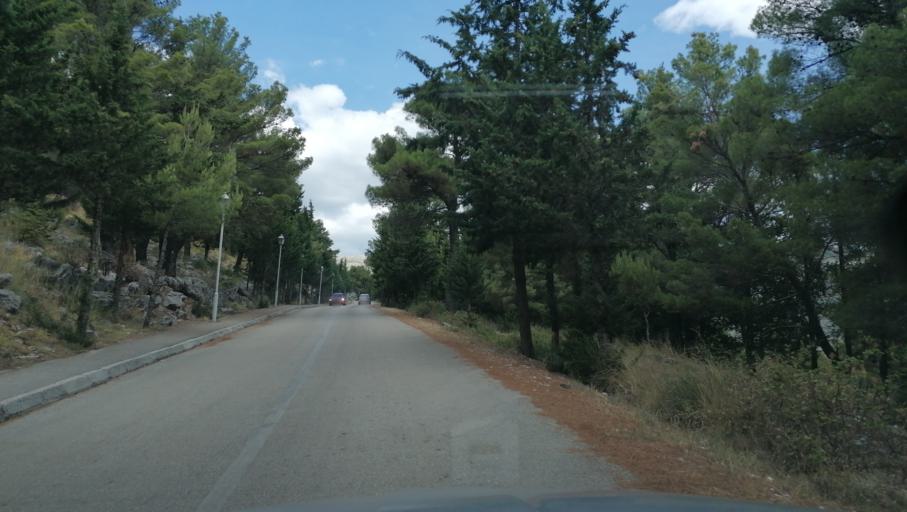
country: BA
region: Republika Srpska
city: Trebinje
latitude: 42.7089
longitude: 18.3625
